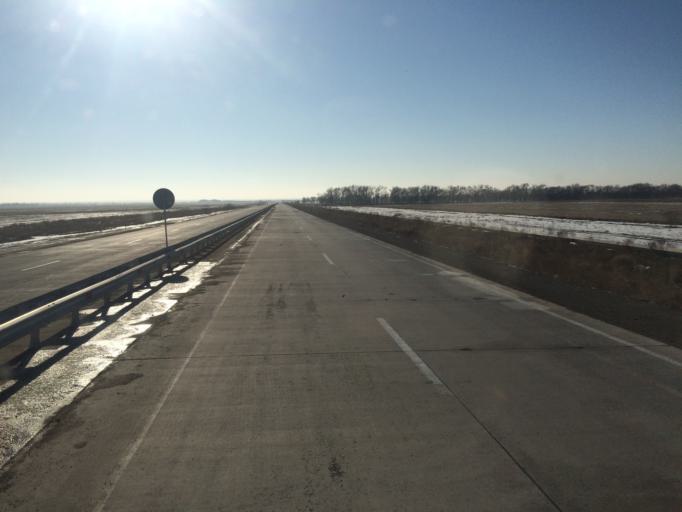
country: KG
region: Chuy
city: Sokuluk
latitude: 43.3001
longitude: 74.2514
